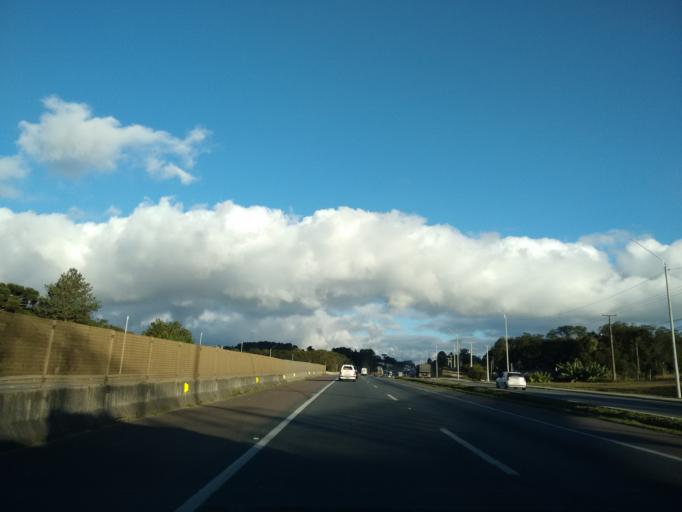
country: BR
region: Parana
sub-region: Sao Jose Dos Pinhais
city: Sao Jose dos Pinhais
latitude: -25.6998
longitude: -49.1435
